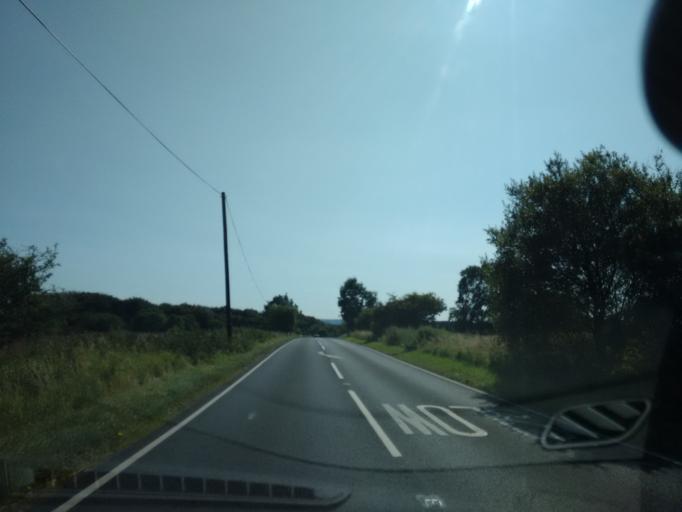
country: GB
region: England
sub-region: Northumberland
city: Corbridge
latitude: 55.0057
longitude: -2.0211
